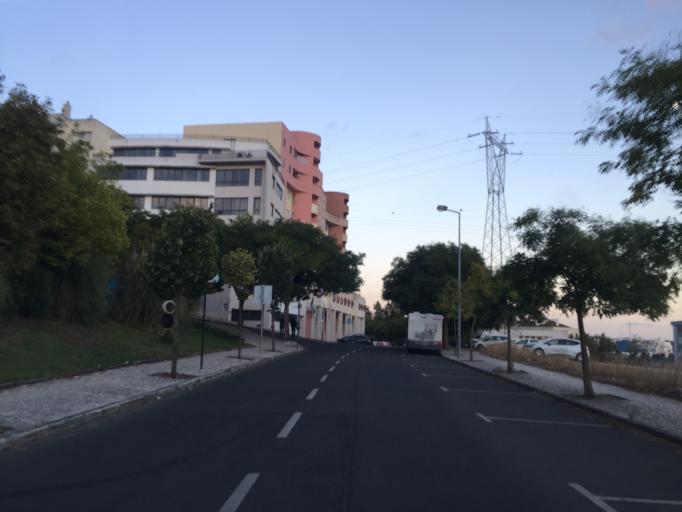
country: PT
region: Lisbon
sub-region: Odivelas
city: Odivelas
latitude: 38.7976
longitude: -9.1832
